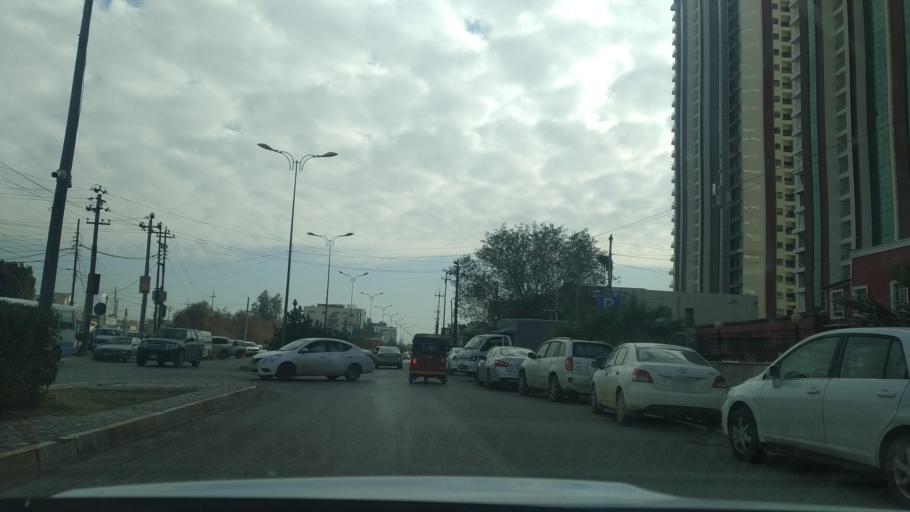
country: IQ
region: Arbil
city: Erbil
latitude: 36.1805
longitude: 44.0253
